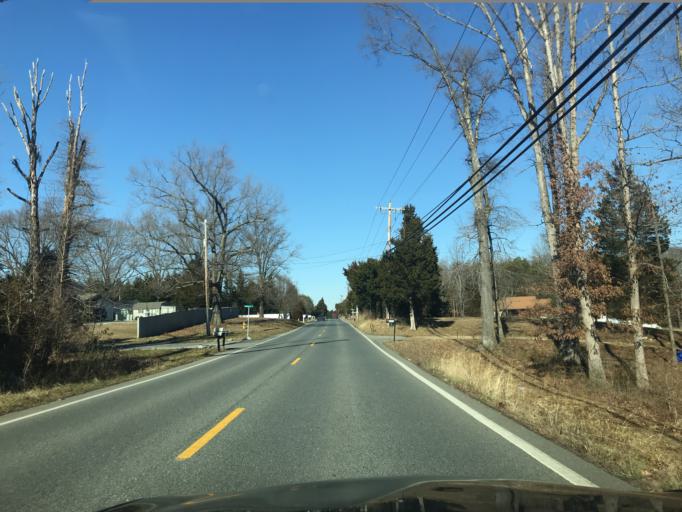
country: US
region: Maryland
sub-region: Charles County
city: Bennsville
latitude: 38.6290
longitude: -77.0150
